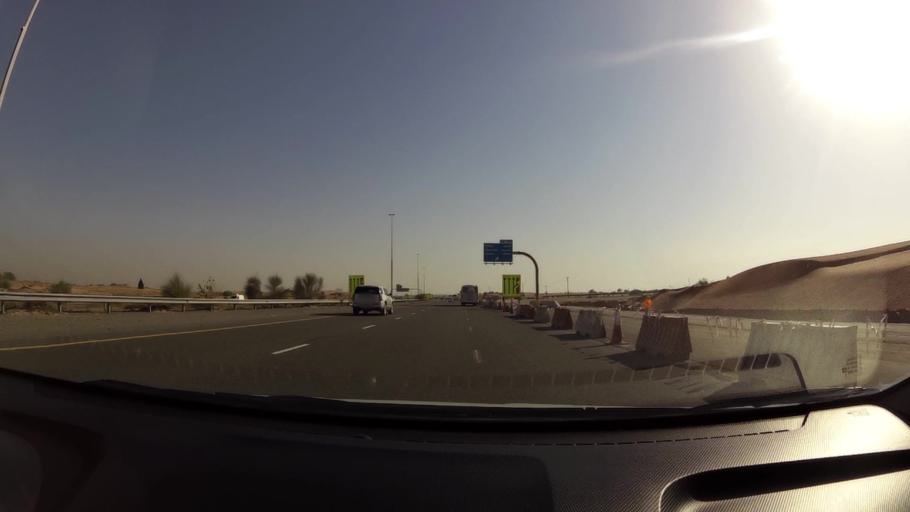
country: AE
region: Umm al Qaywayn
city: Umm al Qaywayn
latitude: 25.4400
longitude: 55.6022
